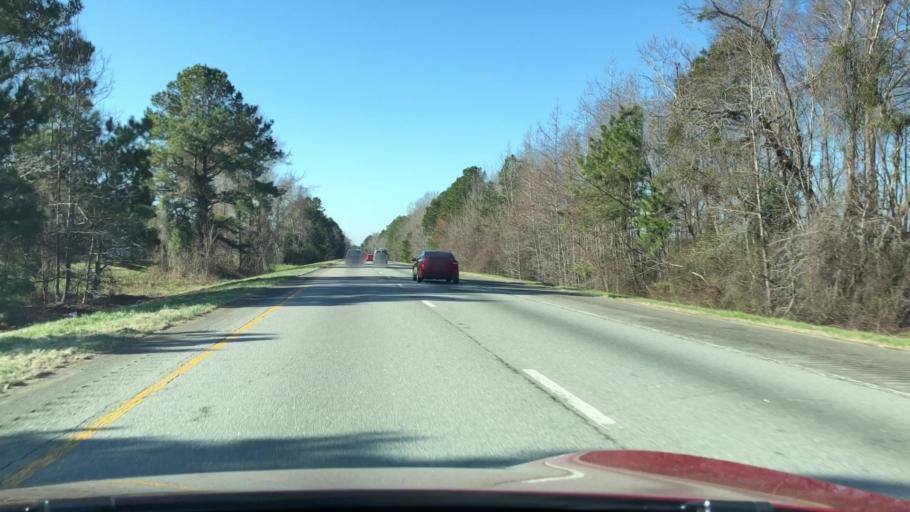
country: US
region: South Carolina
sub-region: Clarendon County
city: Manning
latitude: 33.5763
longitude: -80.3762
